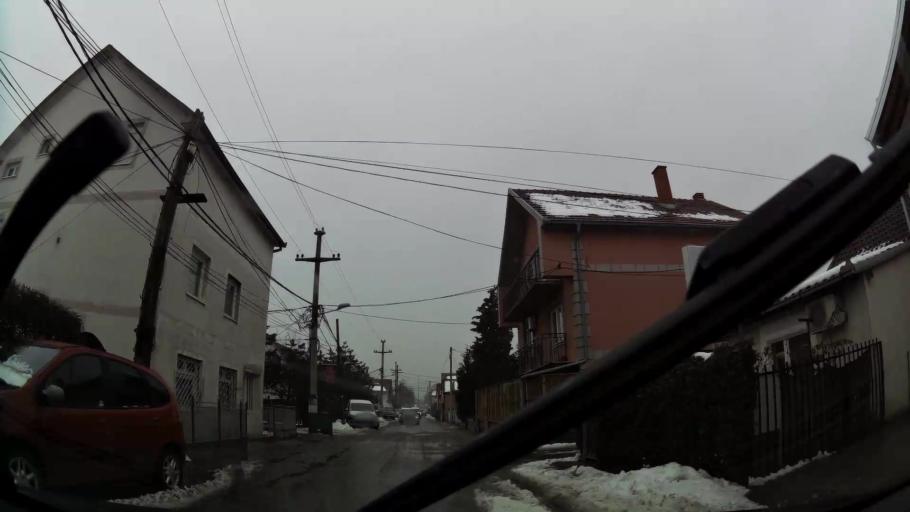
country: RS
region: Central Serbia
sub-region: Belgrade
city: Zemun
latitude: 44.8440
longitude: 20.3672
